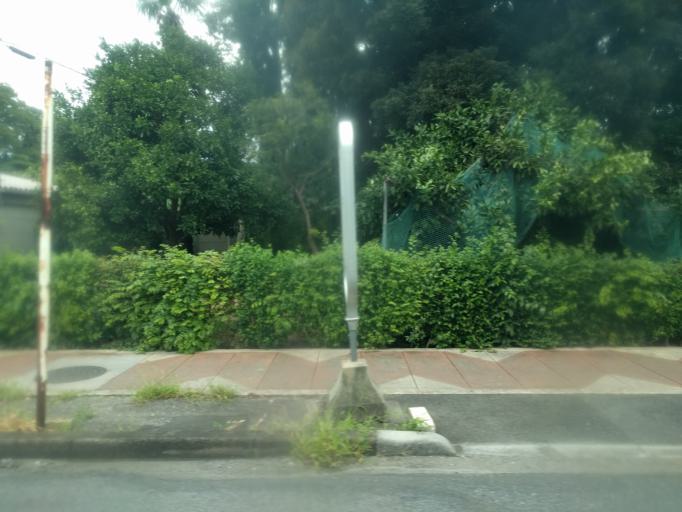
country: JP
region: Saitama
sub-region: Kawaguchi-shi
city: Hatogaya-honcho
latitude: 35.8258
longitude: 139.7341
